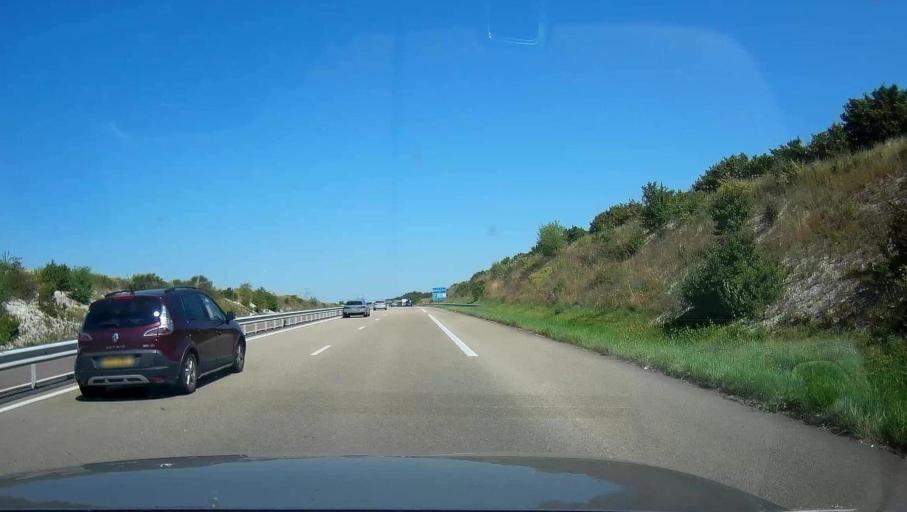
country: FR
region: Champagne-Ardenne
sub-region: Departement de l'Aube
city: Creney-pres-Troyes
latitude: 48.3228
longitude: 4.1658
